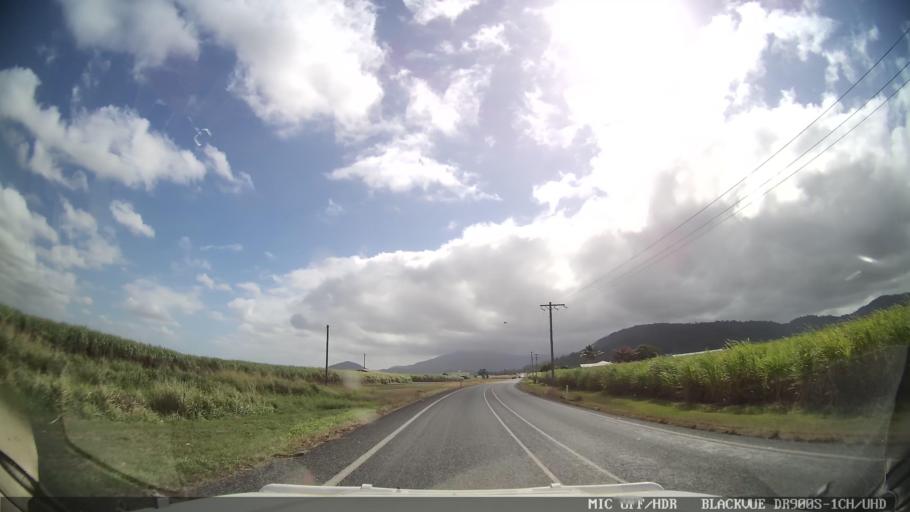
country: AU
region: Queensland
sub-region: Whitsunday
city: Red Hill
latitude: -20.3447
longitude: 148.5527
